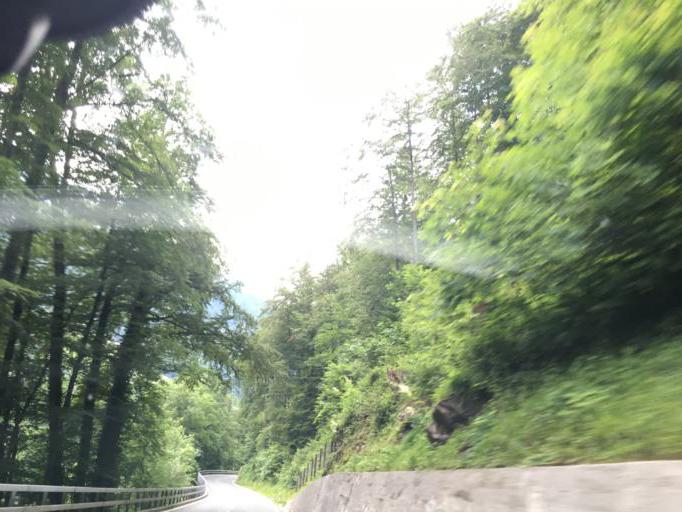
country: CH
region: Obwalden
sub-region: Obwalden
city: Engelberg
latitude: 46.8527
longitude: 8.3728
